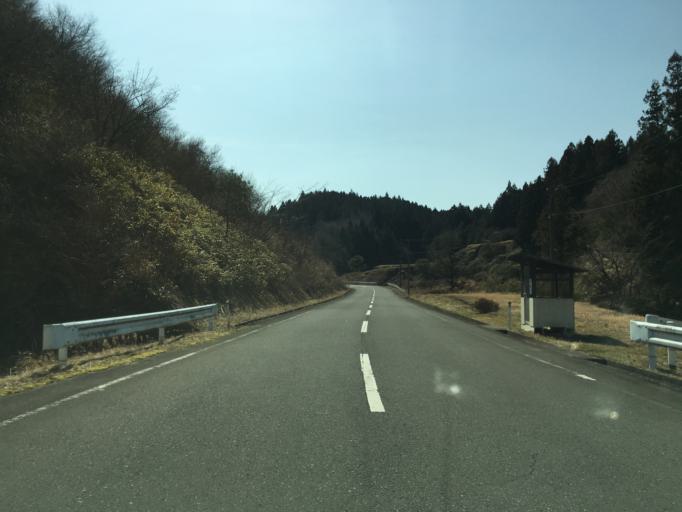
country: JP
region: Fukushima
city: Ishikawa
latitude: 37.1031
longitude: 140.4371
